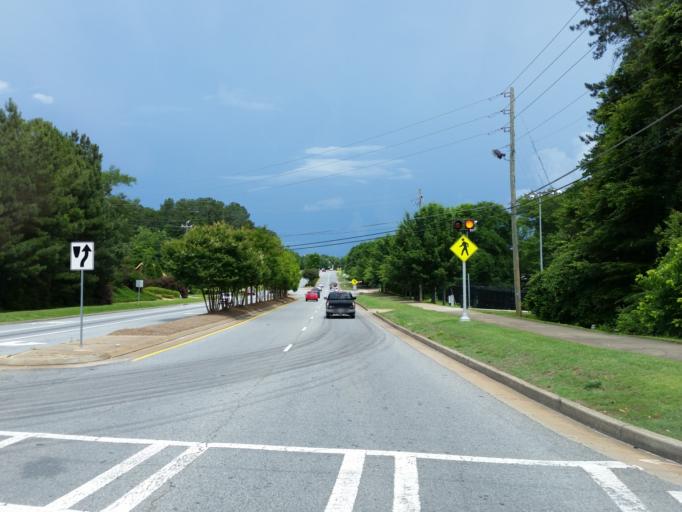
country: US
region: Georgia
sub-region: Fulton County
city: Alpharetta
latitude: 34.0729
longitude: -84.3108
